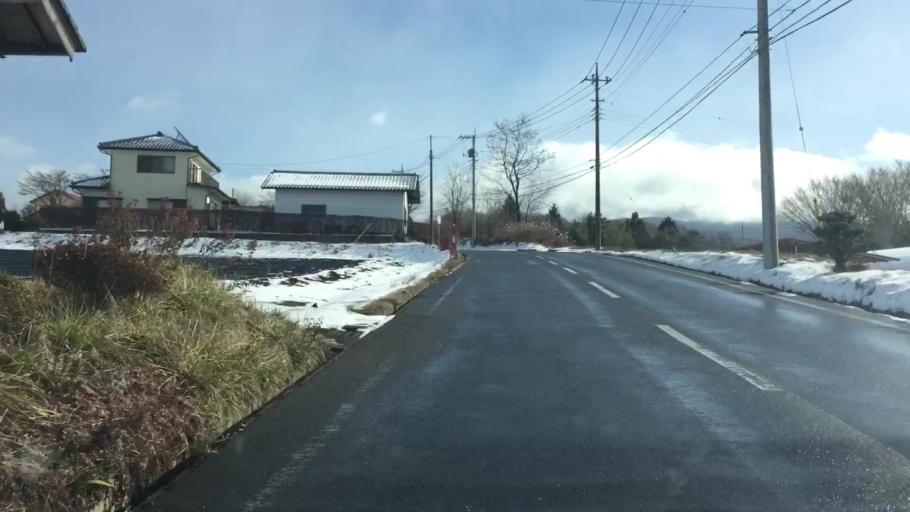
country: JP
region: Gunma
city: Numata
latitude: 36.6061
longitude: 139.0937
